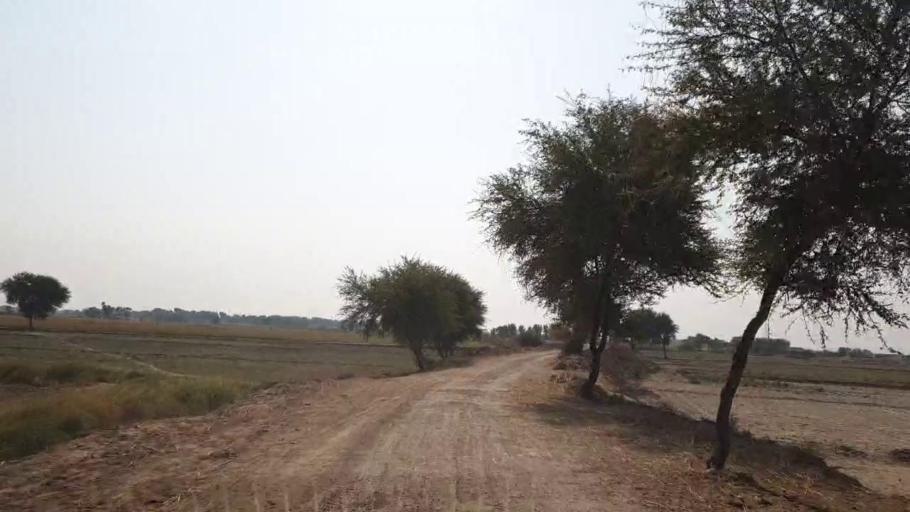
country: PK
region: Sindh
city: Tando Muhammad Khan
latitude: 25.0228
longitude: 68.4171
